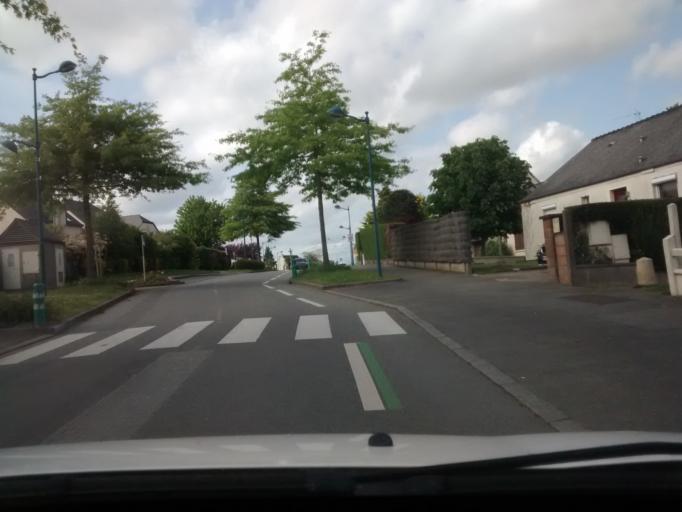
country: FR
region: Brittany
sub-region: Departement d'Ille-et-Vilaine
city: Chateaugiron
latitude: 48.0605
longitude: -1.5245
